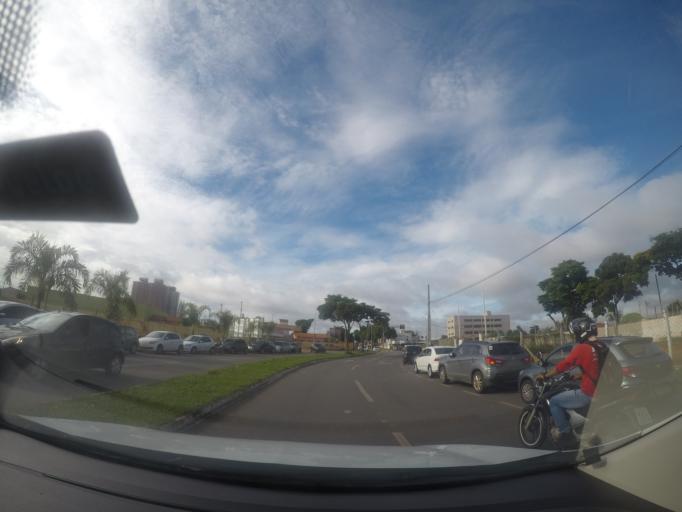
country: BR
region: Goias
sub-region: Goiania
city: Goiania
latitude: -16.6919
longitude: -49.3110
